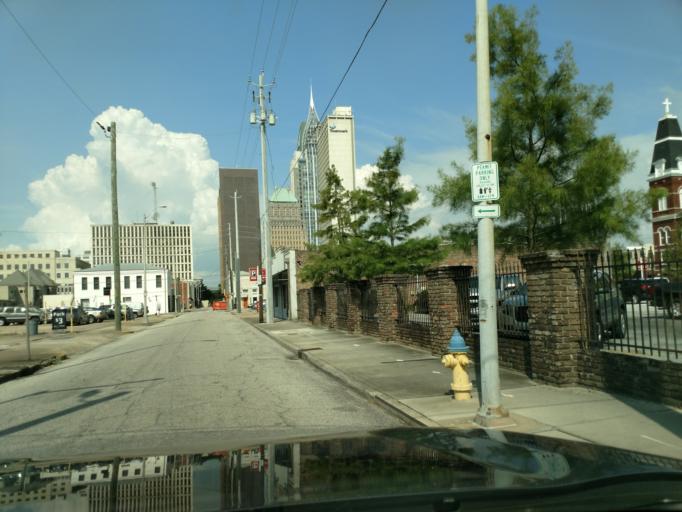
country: US
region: Alabama
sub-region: Mobile County
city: Mobile
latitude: 30.6923
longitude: -88.0455
